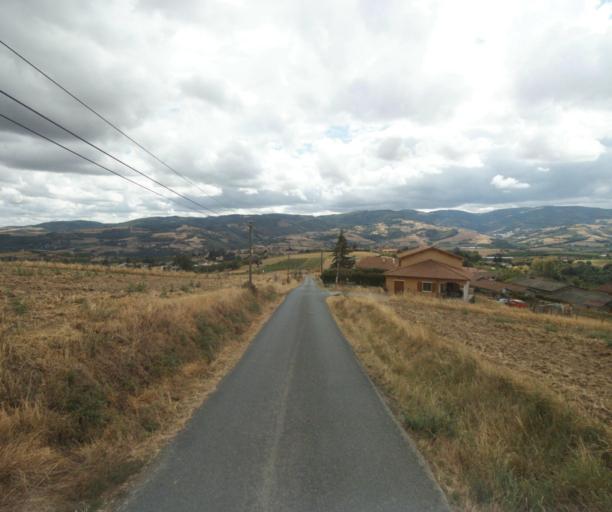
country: FR
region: Rhone-Alpes
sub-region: Departement du Rhone
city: Bessenay
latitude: 45.7817
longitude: 4.5368
